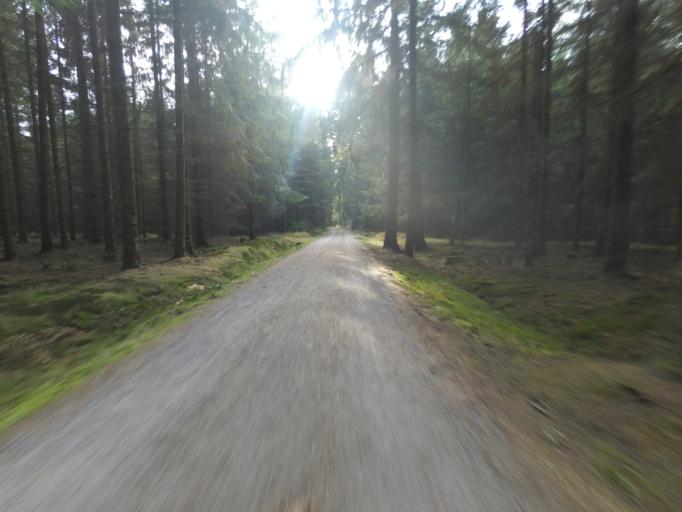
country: DE
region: Saxony
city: Radeberg
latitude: 51.0877
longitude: 13.8620
